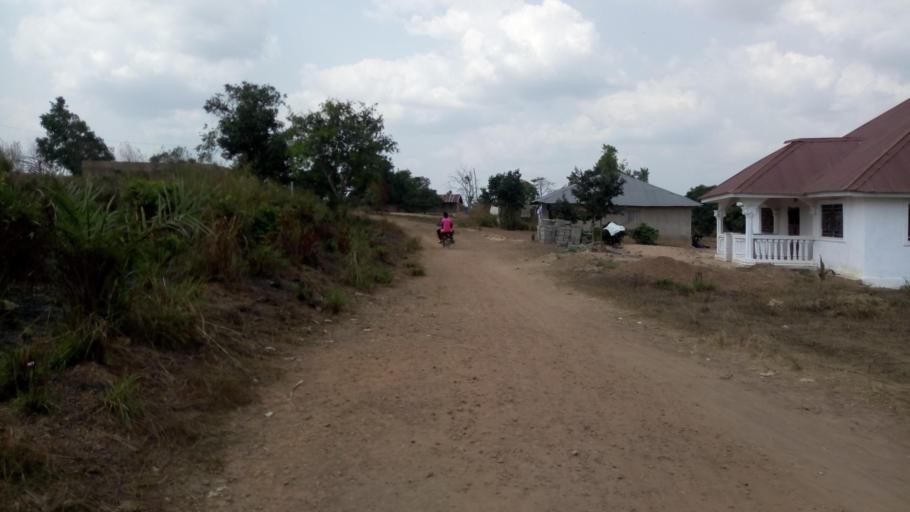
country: SL
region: Southern Province
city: Mogbwemo
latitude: 7.7934
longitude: -12.3027
